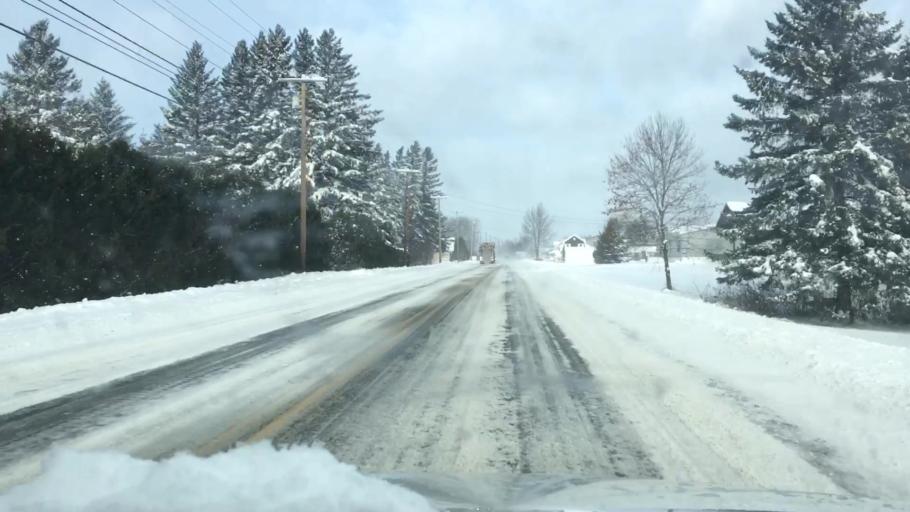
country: US
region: Maine
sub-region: Aroostook County
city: Van Buren
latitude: 47.1808
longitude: -67.9519
